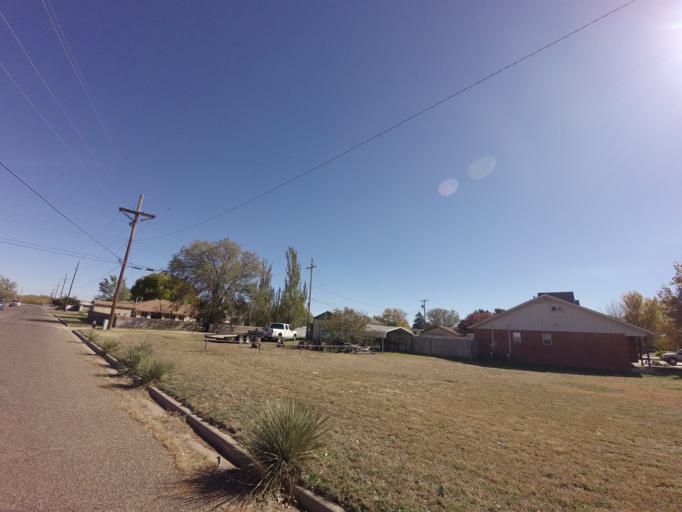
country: US
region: New Mexico
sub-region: Curry County
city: Clovis
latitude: 34.4302
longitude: -103.2000
